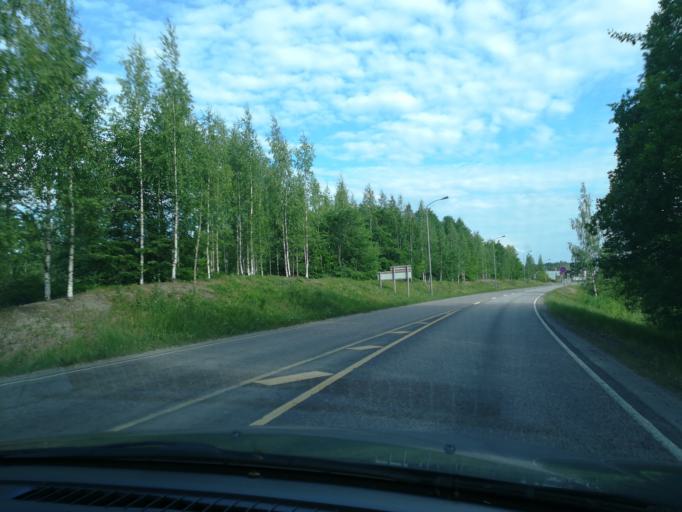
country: FI
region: South Karelia
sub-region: Imatra
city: Imatra
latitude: 61.1537
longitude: 28.8048
